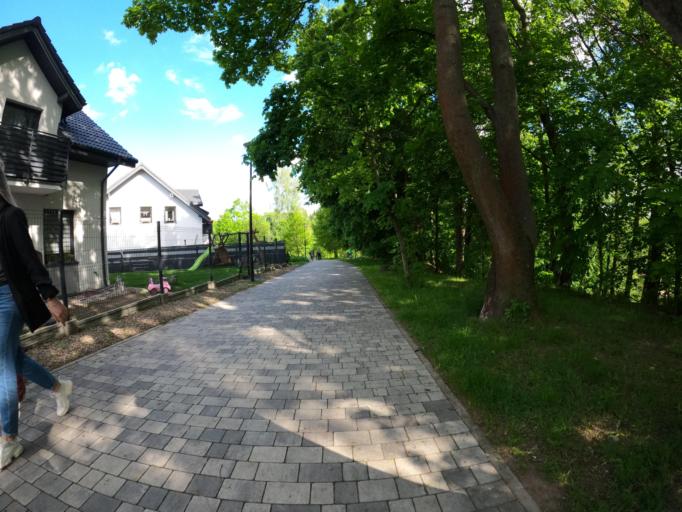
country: PL
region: Warmian-Masurian Voivodeship
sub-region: Powiat lidzbarski
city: Lidzbark Warminski
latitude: 54.1285
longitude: 20.5884
